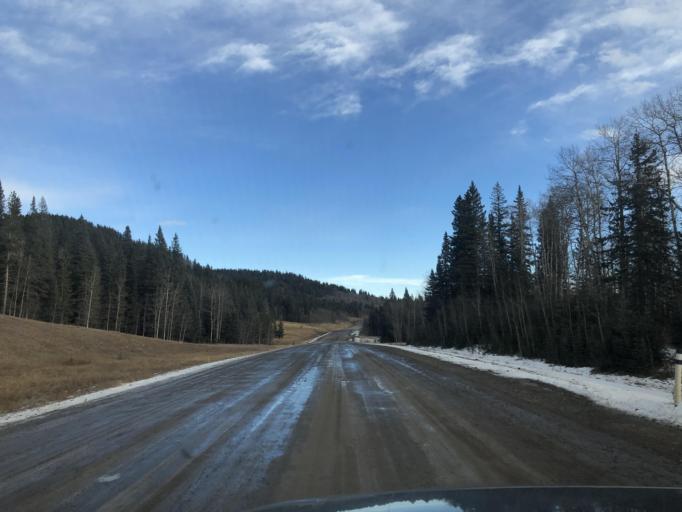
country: CA
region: Alberta
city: Cochrane
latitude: 51.0435
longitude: -114.7654
